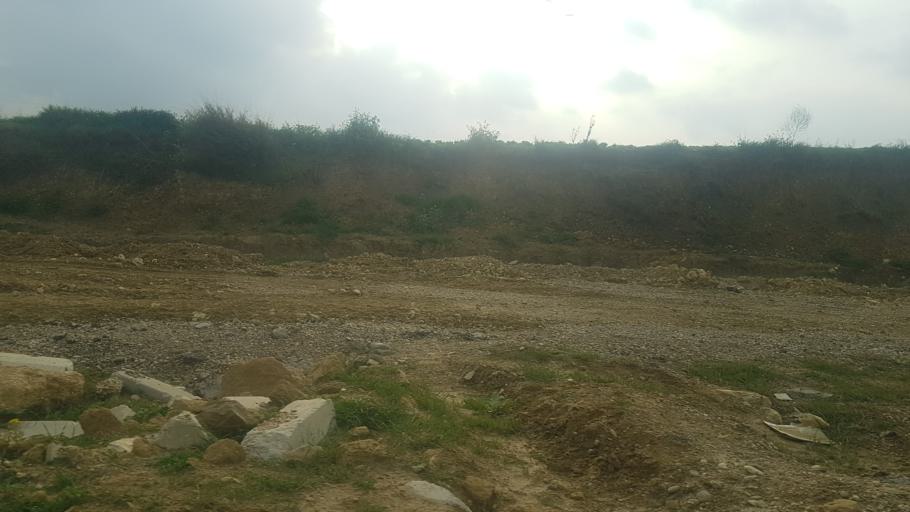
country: TR
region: Adana
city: Seyhan
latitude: 37.0485
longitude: 35.2101
